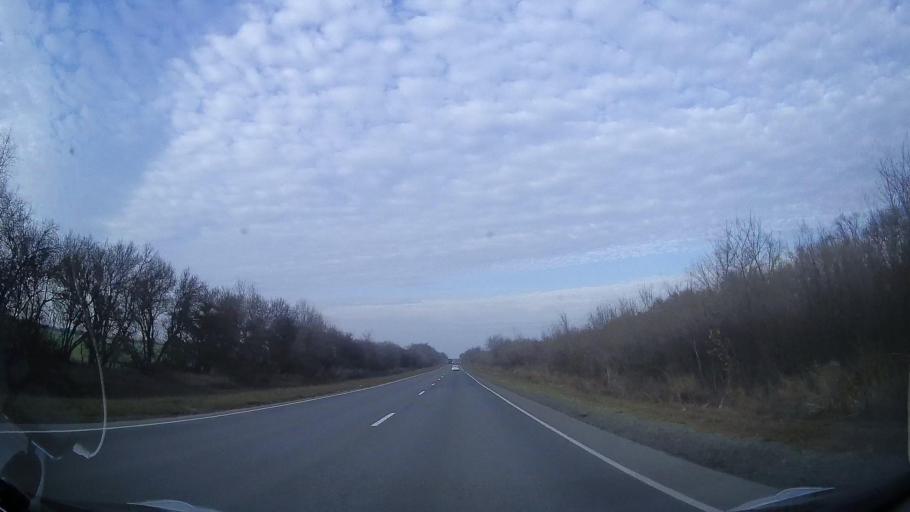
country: RU
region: Rostov
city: Bagayevskaya
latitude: 47.1357
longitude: 40.2767
